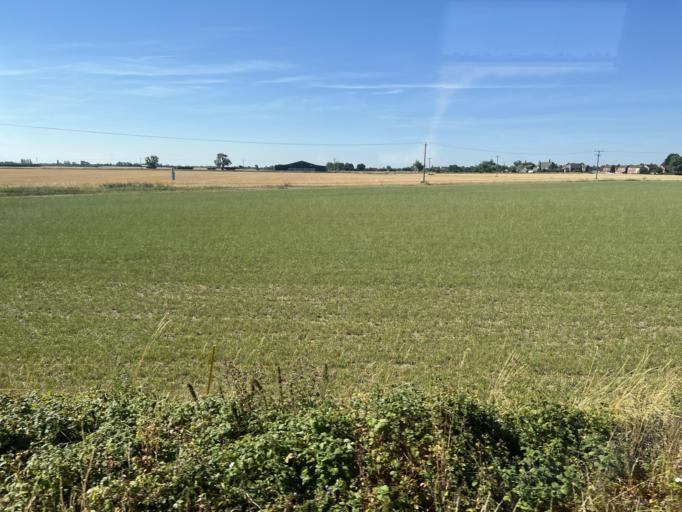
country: GB
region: England
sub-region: Lincolnshire
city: Heckington
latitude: 52.9750
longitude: -0.2815
